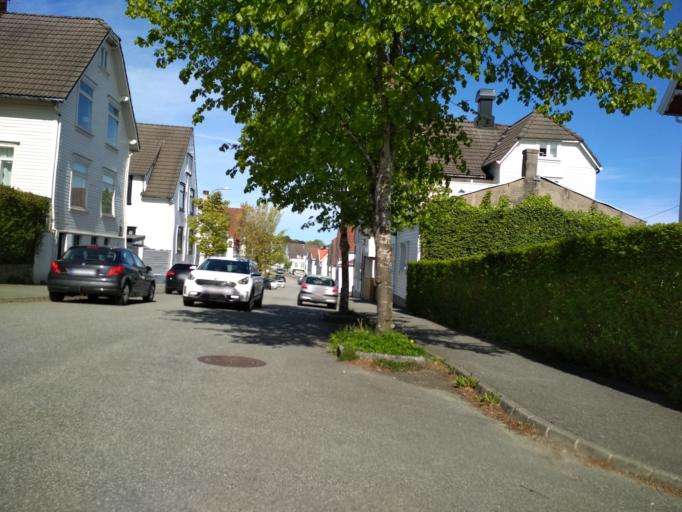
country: NO
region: Rogaland
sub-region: Stavanger
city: Stavanger
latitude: 58.9595
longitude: 5.7353
